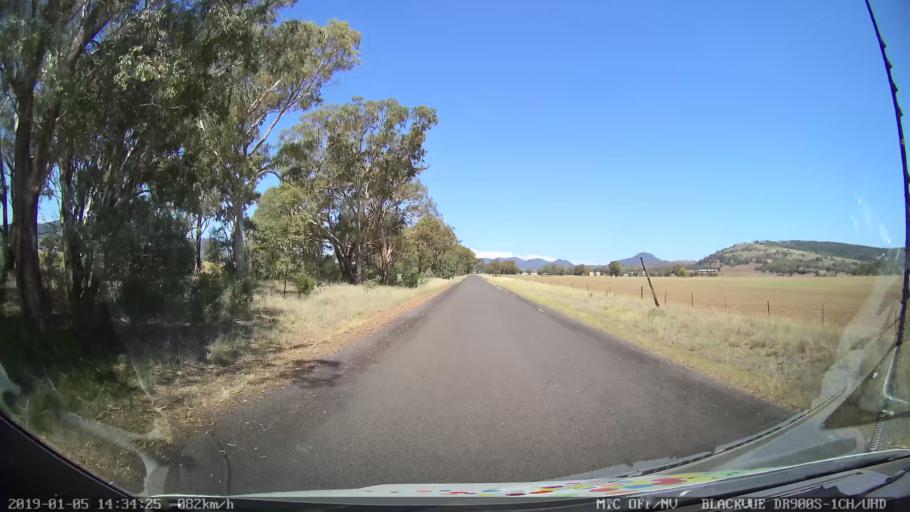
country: AU
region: New South Wales
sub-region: Tamworth Municipality
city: Phillip
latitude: -31.2327
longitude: 150.6413
